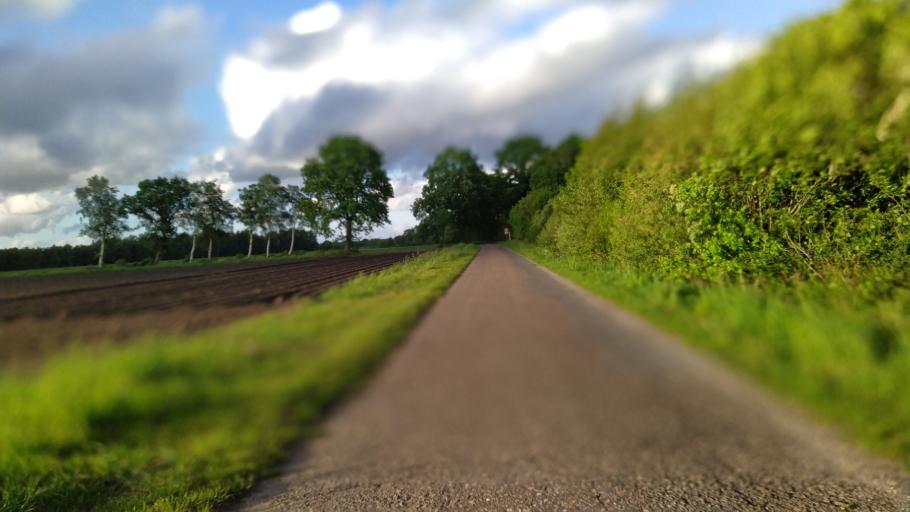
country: DE
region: Lower Saxony
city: Brest
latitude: 53.4718
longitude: 9.4003
